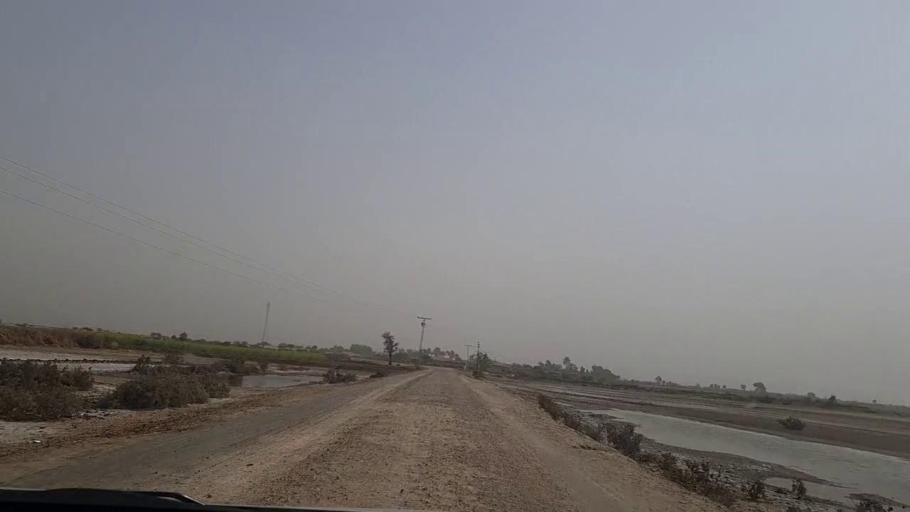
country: PK
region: Sindh
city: Pithoro
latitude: 25.4562
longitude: 69.2322
